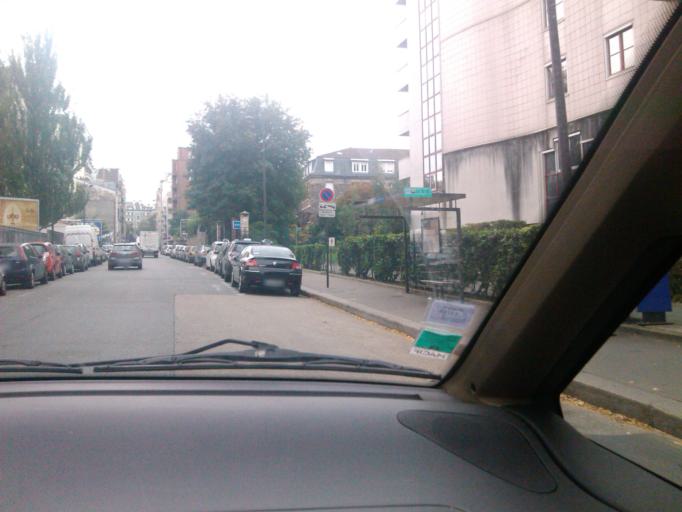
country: FR
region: Ile-de-France
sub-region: Departement des Hauts-de-Seine
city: Montrouge
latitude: 48.8273
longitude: 2.3204
